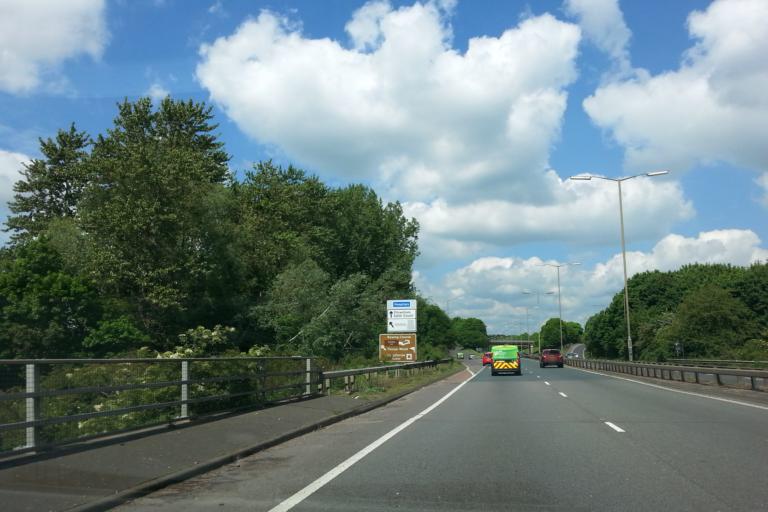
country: GB
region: England
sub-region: Peterborough
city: Peterborough
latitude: 52.5615
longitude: -0.2811
